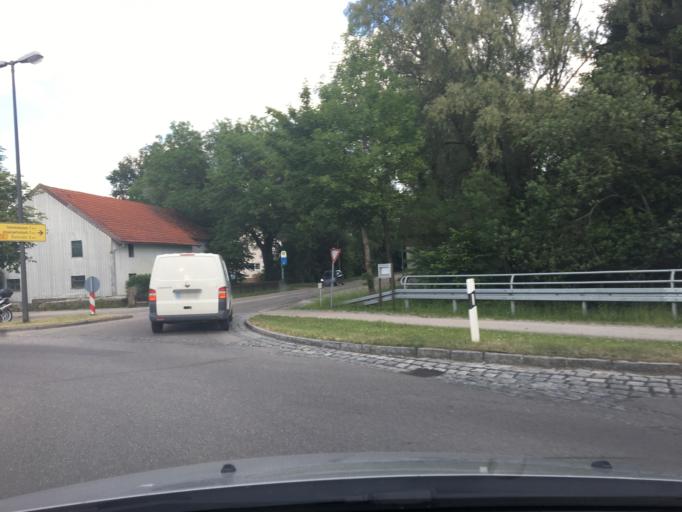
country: DE
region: Bavaria
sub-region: Upper Bavaria
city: Hebertshausen
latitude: 48.3153
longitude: 11.4921
